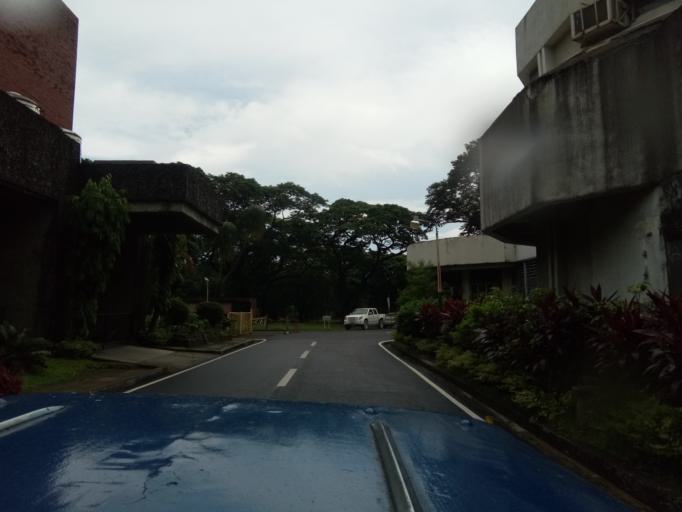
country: PH
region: Metro Manila
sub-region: Quezon City
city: Quezon City
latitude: 14.6569
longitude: 121.0658
